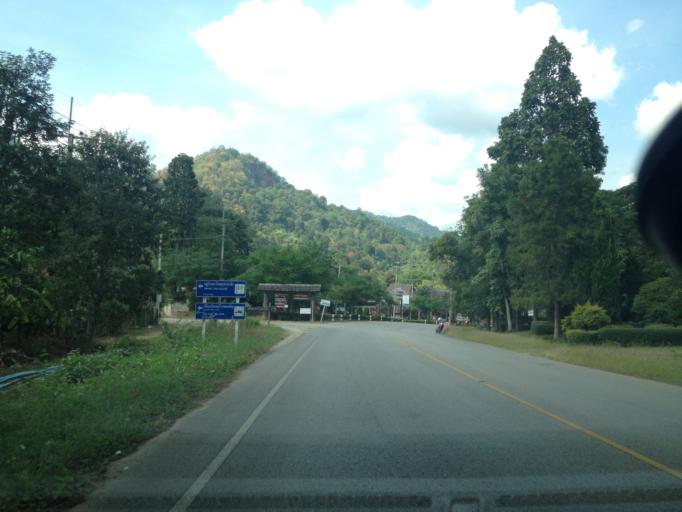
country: TH
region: Chiang Mai
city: Hang Dong
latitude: 18.7760
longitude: 98.8549
